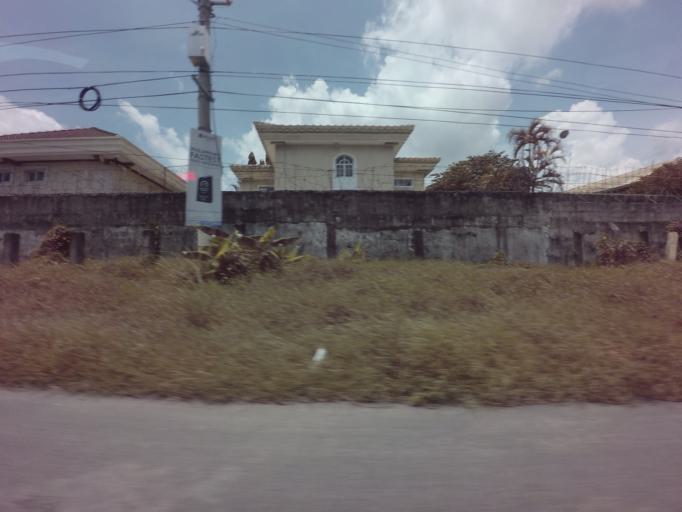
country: PH
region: Calabarzon
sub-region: Province of Laguna
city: San Pedro
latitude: 14.3919
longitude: 121.0095
